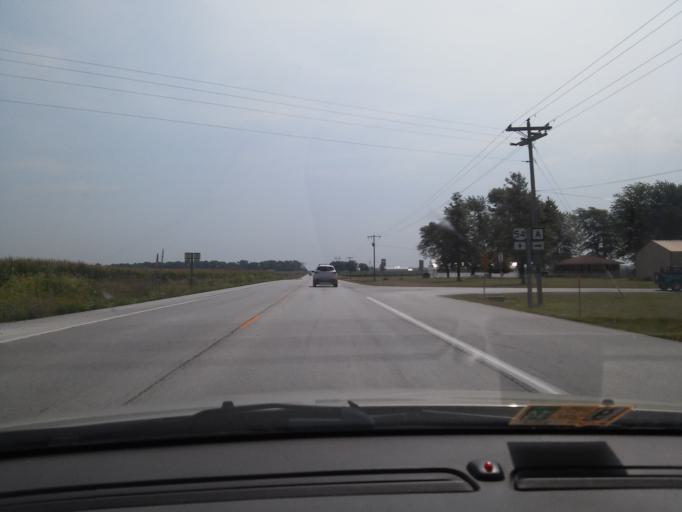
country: US
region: Missouri
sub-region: Audrain County
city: Mexico
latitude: 39.1638
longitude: -91.7621
